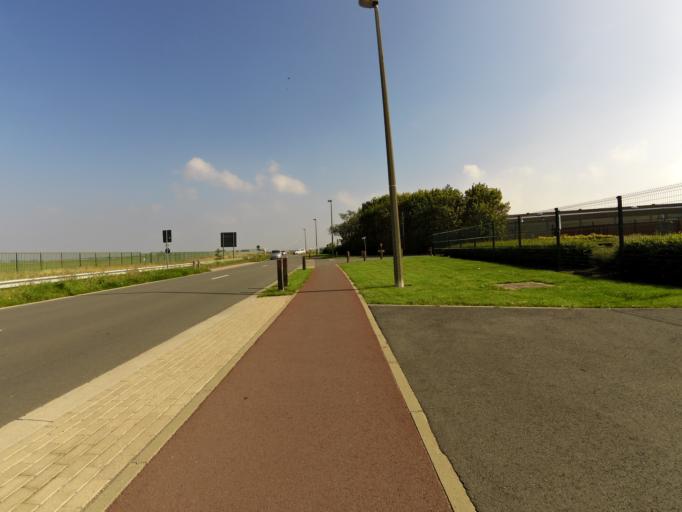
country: BE
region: Flanders
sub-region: Provincie West-Vlaanderen
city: Middelkerke
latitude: 51.1947
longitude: 2.8455
